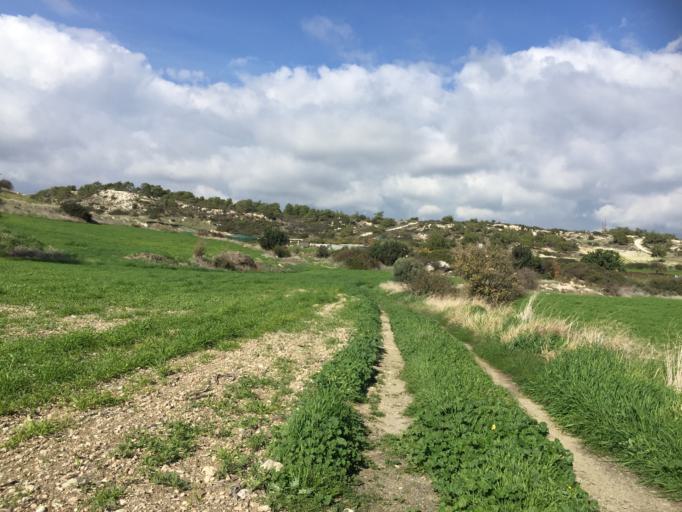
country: CY
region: Larnaka
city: Agios Tychon
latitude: 34.7408
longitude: 33.1411
